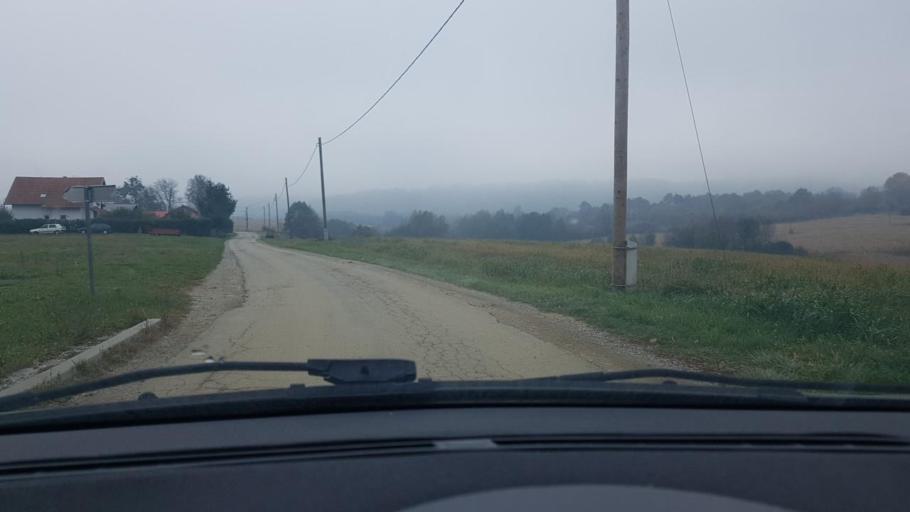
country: HR
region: Krapinsko-Zagorska
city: Zlatar
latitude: 46.1093
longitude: 16.1779
